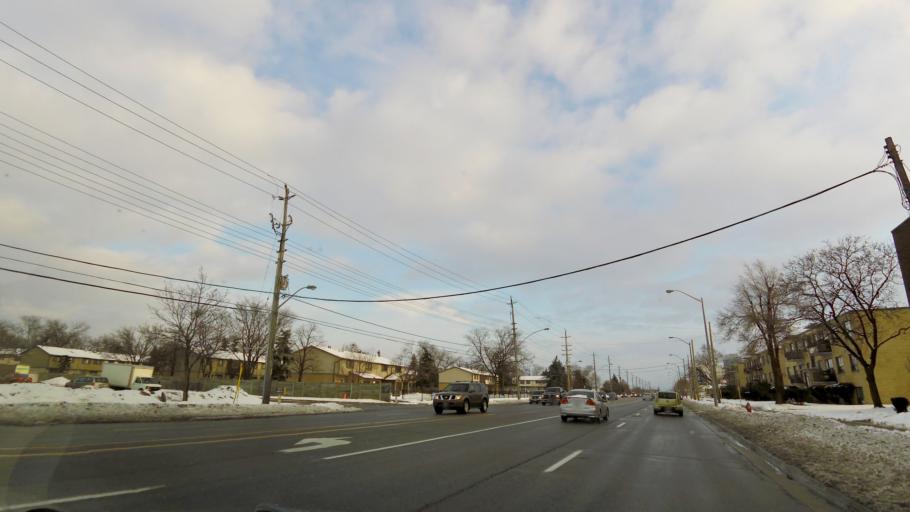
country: CA
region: Ontario
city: Brampton
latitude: 43.7011
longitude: -79.7568
